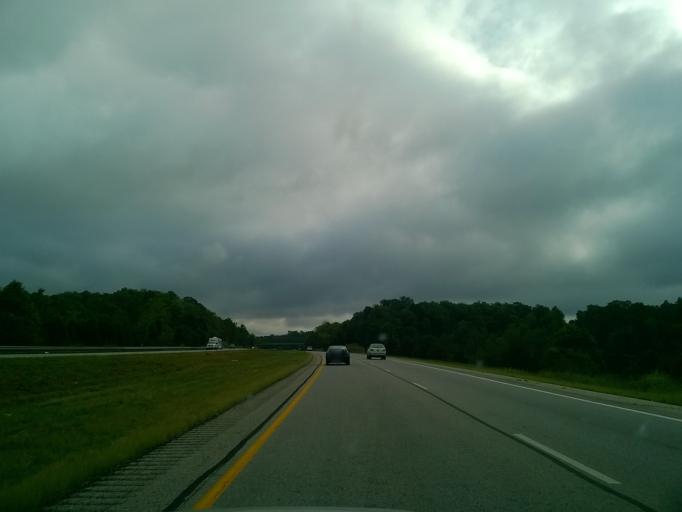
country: US
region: Indiana
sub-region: Harrison County
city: Corydon
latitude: 38.2448
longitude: -86.0912
